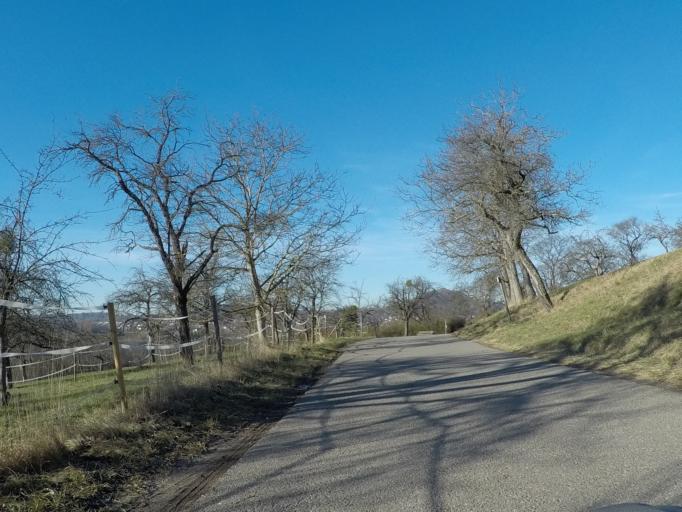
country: DE
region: Baden-Wuerttemberg
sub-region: Tuebingen Region
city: Pfullingen
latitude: 48.4542
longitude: 9.2375
